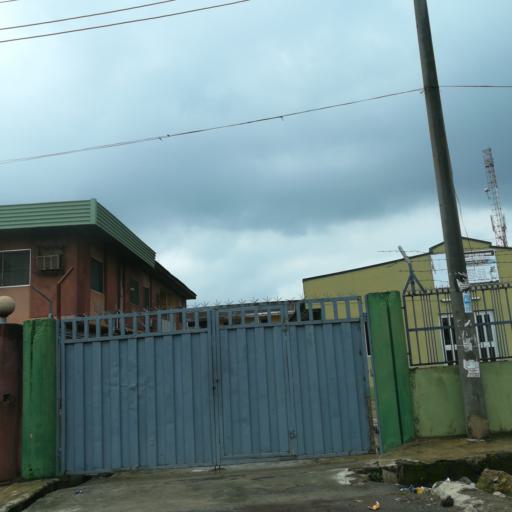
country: NG
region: Lagos
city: Agege
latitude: 6.5995
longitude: 3.2964
